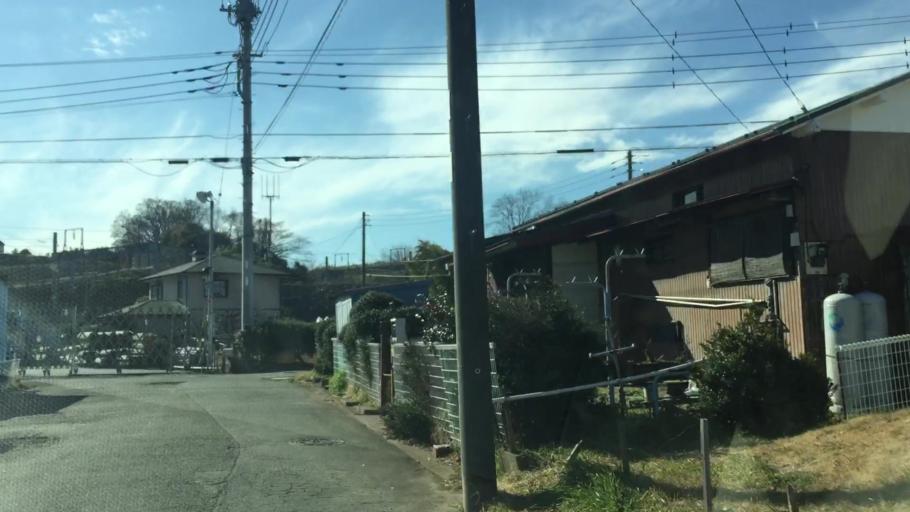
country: JP
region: Kanagawa
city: Yokohama
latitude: 35.4852
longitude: 139.5865
